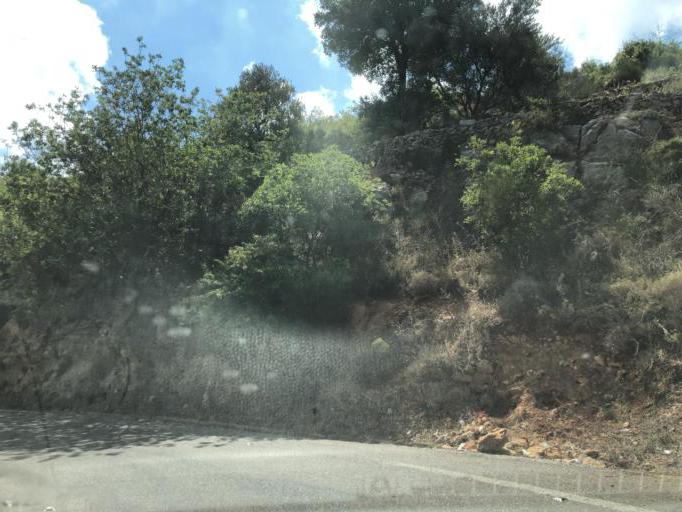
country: LB
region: Mont-Liban
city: Beit ed Dine
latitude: 33.7024
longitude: 35.5786
